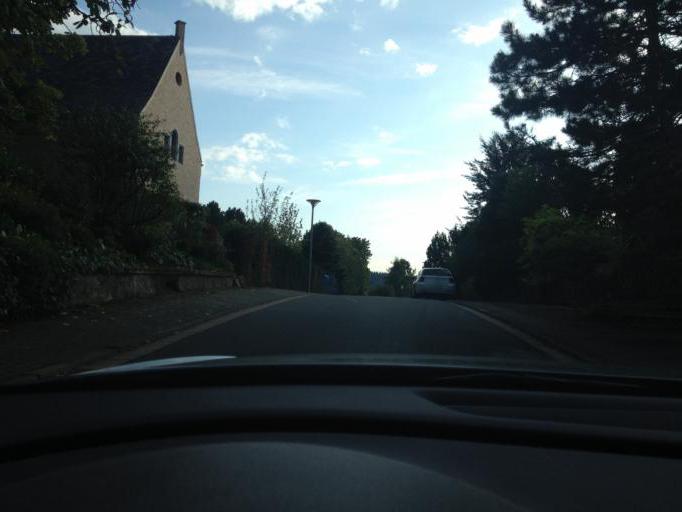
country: DE
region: Saarland
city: Sankt Wendel
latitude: 49.4585
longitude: 7.1741
